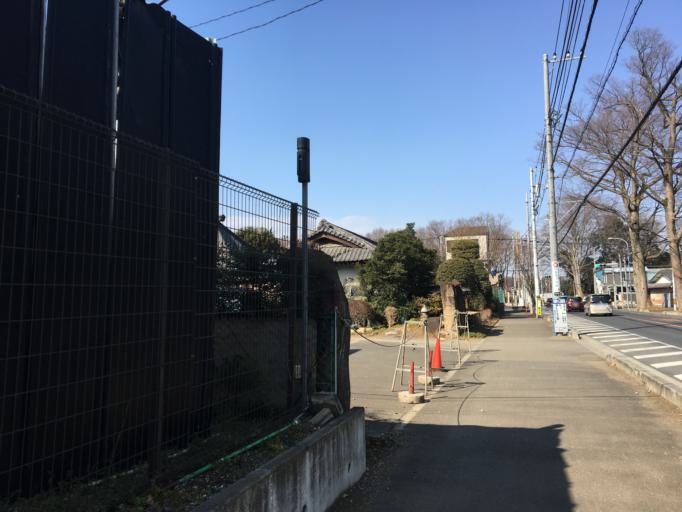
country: JP
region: Saitama
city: Oi
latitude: 35.8353
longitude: 139.4994
